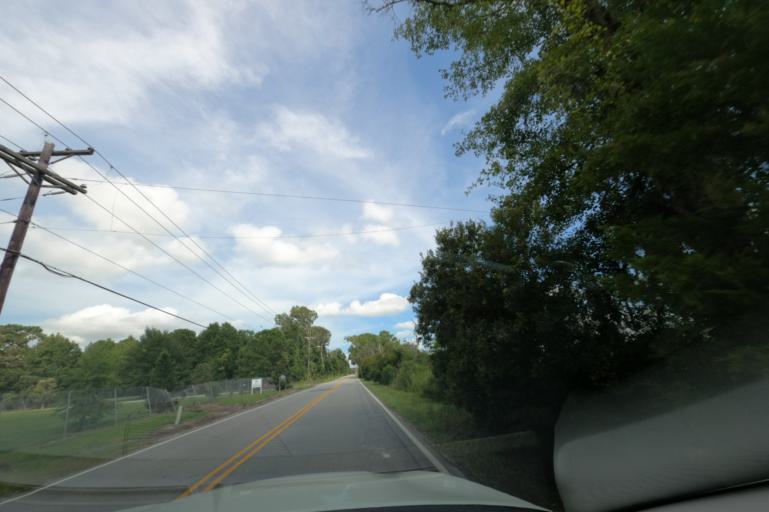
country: US
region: South Carolina
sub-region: Charleston County
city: Shell Point
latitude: 32.8019
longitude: -80.1152
